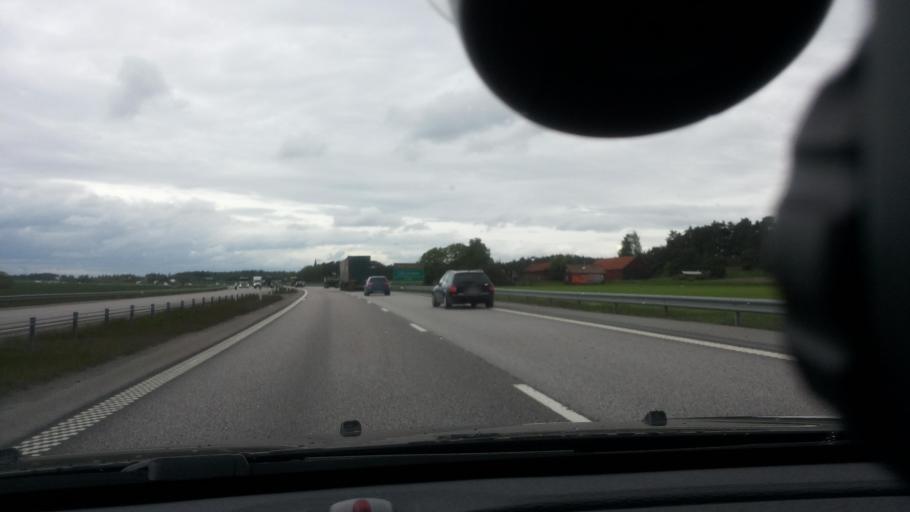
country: SE
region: Uppsala
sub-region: Uppsala Kommun
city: Saevja
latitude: 59.8162
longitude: 17.7546
